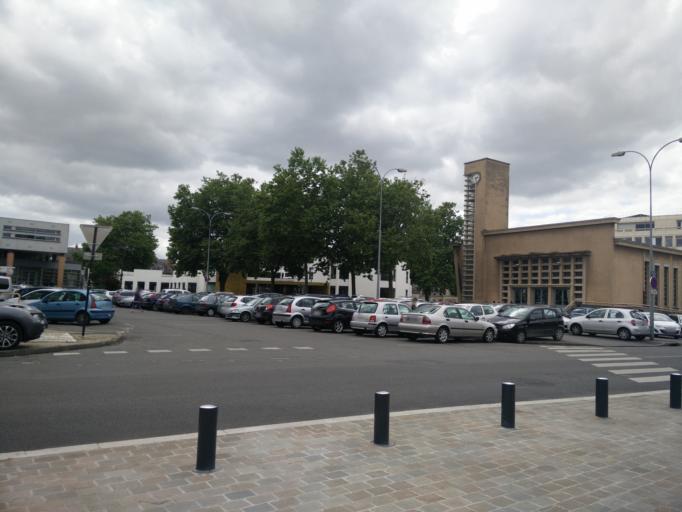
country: FR
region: Auvergne
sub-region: Departement de l'Allier
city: Moulins
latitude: 46.5625
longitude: 3.3306
